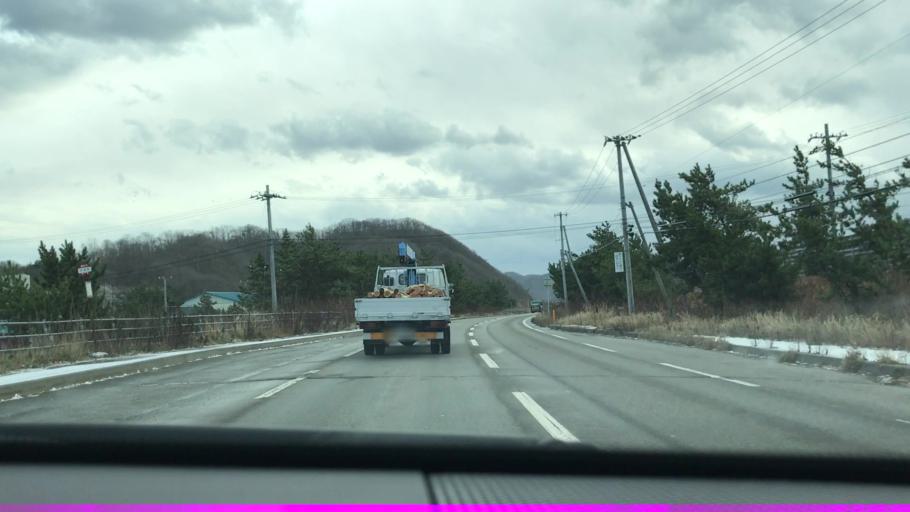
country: JP
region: Hokkaido
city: Shizunai-furukawacho
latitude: 42.3084
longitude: 142.4377
